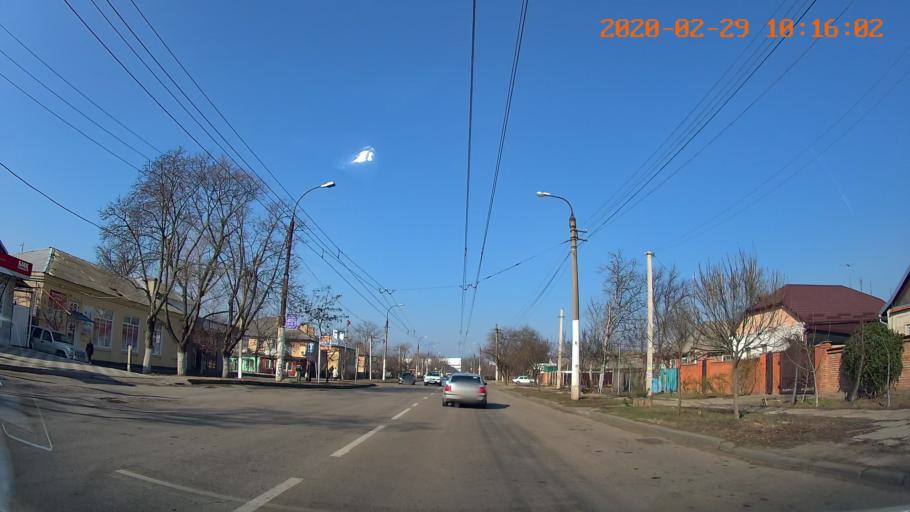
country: MD
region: Telenesti
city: Tiraspolul Nou
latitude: 46.8541
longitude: 29.6328
